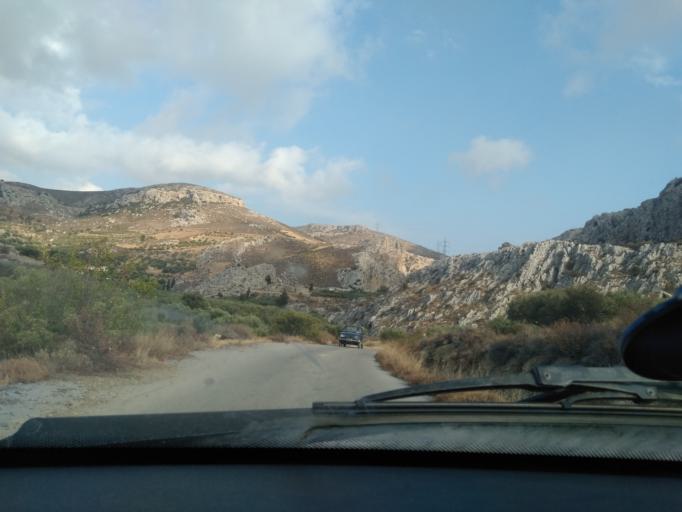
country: GR
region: Crete
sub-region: Nomos Lasithiou
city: Makry-Gialos
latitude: 35.0459
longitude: 26.0536
